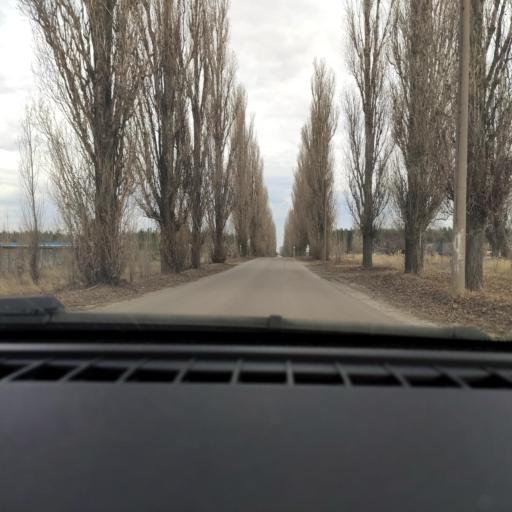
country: RU
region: Voronezj
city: Maslovka
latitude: 51.6013
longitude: 39.2207
